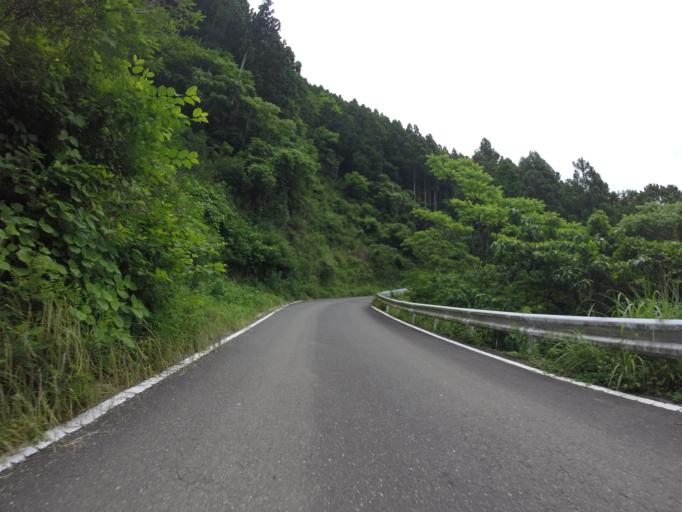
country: JP
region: Shizuoka
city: Shizuoka-shi
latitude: 35.0444
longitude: 138.3090
